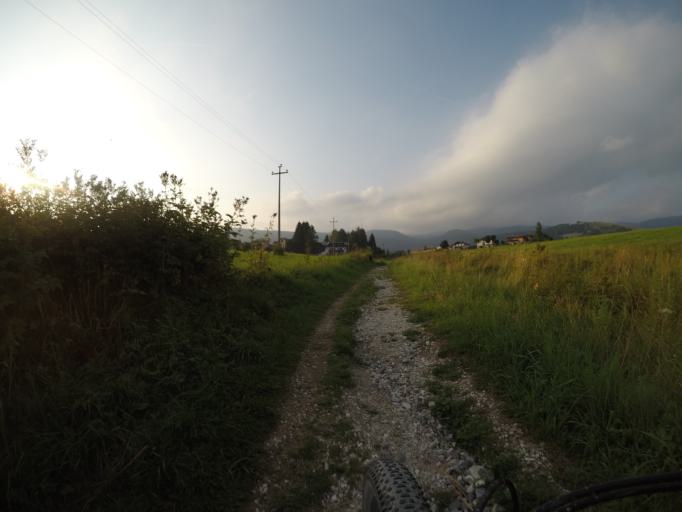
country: IT
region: Veneto
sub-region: Provincia di Vicenza
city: Asiago
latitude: 45.8824
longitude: 11.5005
